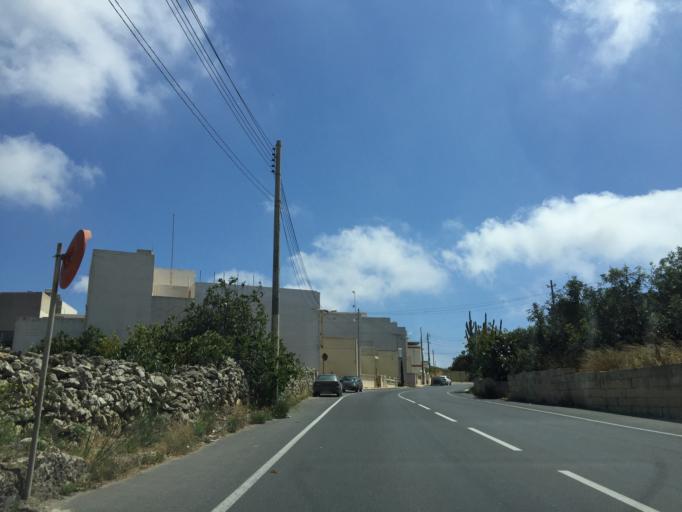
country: MT
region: Dingli
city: Dingli
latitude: 35.8655
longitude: 14.3897
